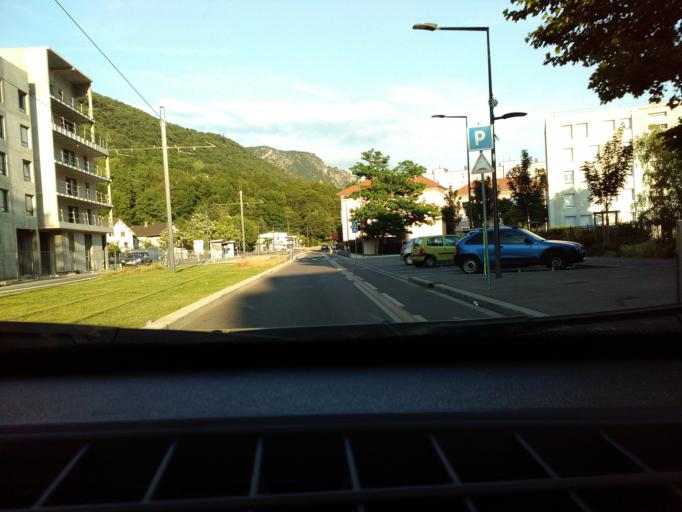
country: FR
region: Rhone-Alpes
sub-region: Departement de l'Isere
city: Fontaine
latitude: 45.2142
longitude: 5.6974
